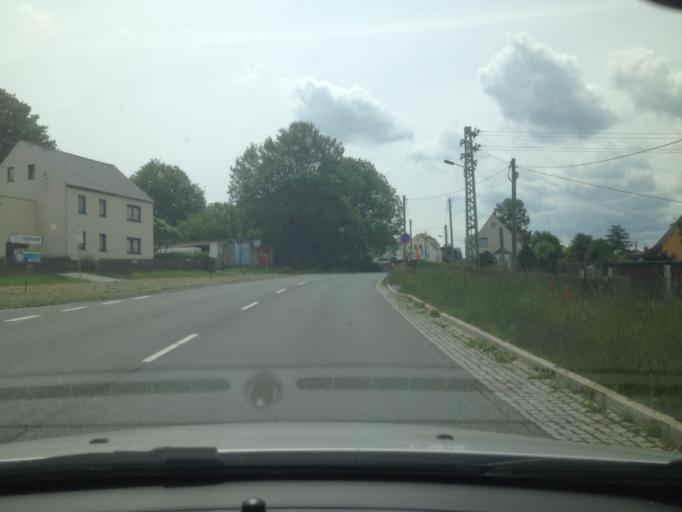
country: DE
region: Saxony
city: Stollberg
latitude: 50.6926
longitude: 12.7681
